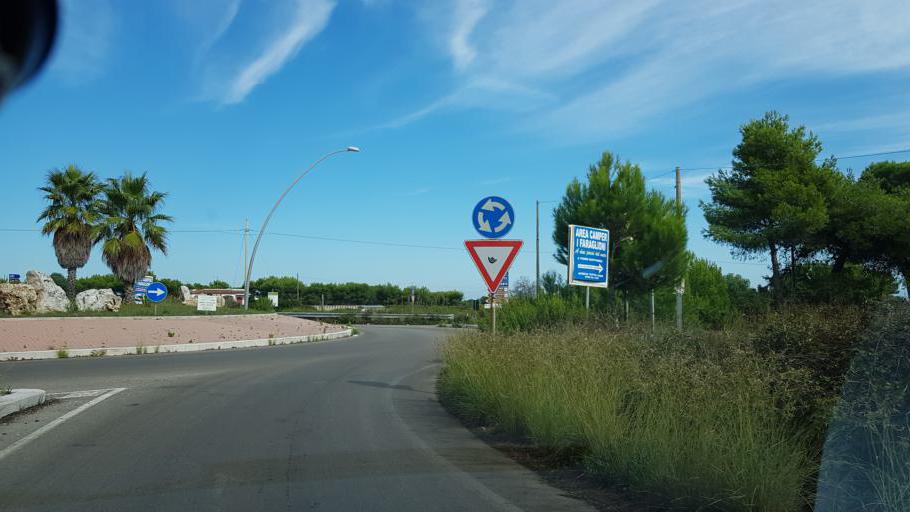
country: IT
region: Apulia
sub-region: Provincia di Lecce
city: Borgagne
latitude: 40.2535
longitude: 18.4389
